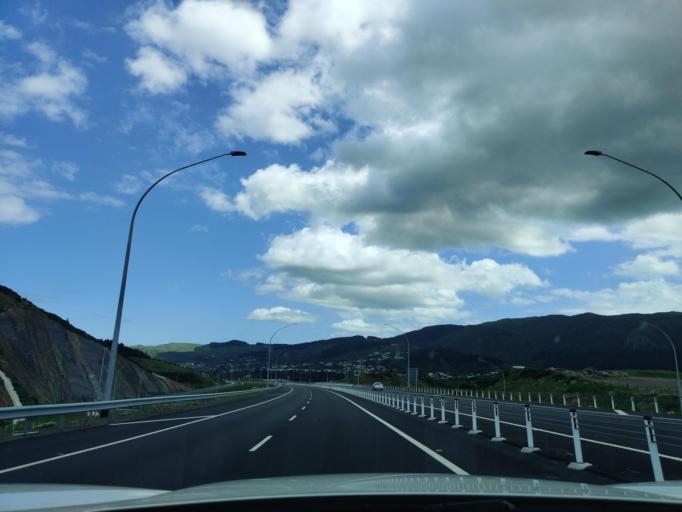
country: NZ
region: Wellington
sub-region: Porirua City
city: Porirua
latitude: -41.1508
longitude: 174.8459
